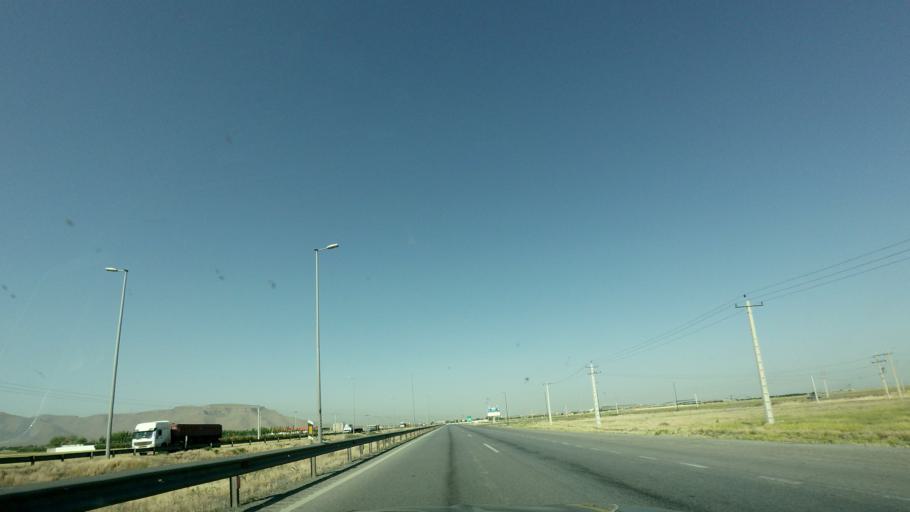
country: IR
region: Markazi
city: Arak
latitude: 34.1573
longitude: 50.0063
